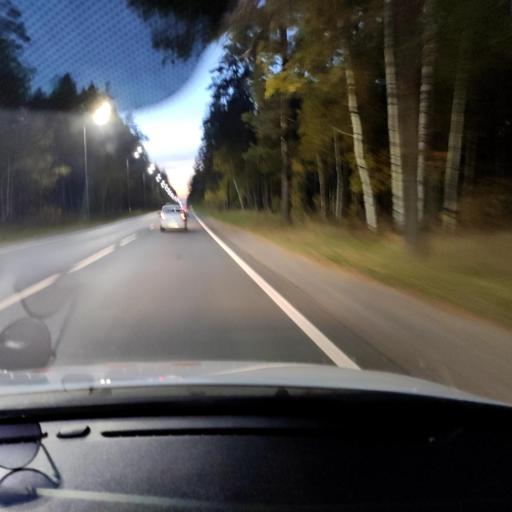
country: RU
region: Tatarstan
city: Stolbishchi
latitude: 55.6357
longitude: 49.0707
